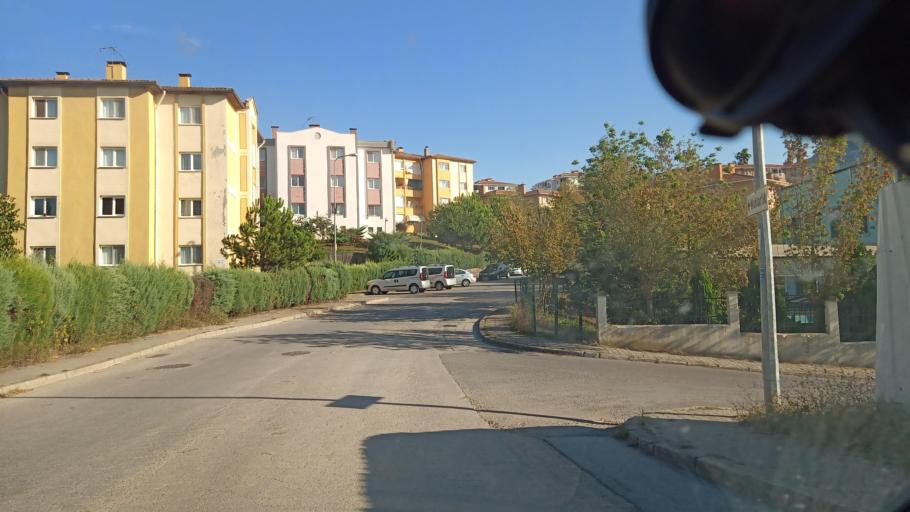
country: TR
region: Kocaeli
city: Kaymaz
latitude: 40.8614
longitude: 30.2869
